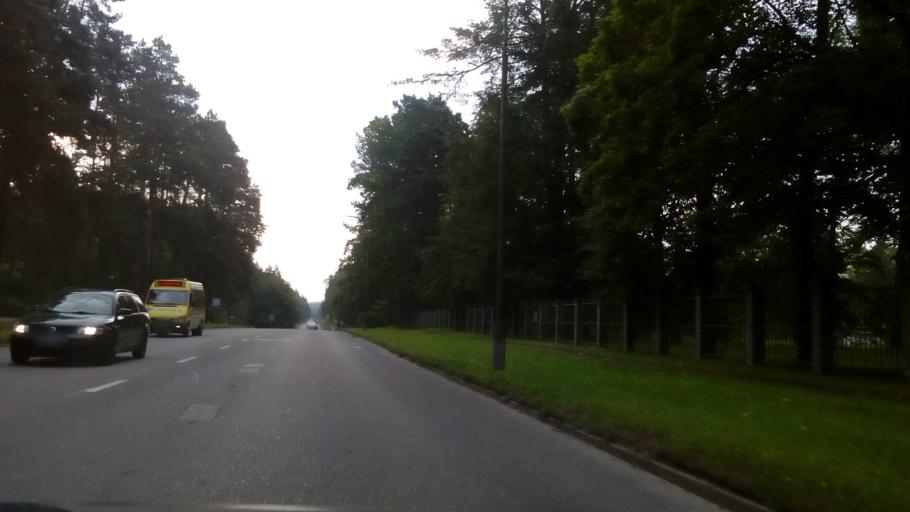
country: LT
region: Alytaus apskritis
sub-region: Alytus
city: Alytus
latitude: 54.3803
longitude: 24.0608
